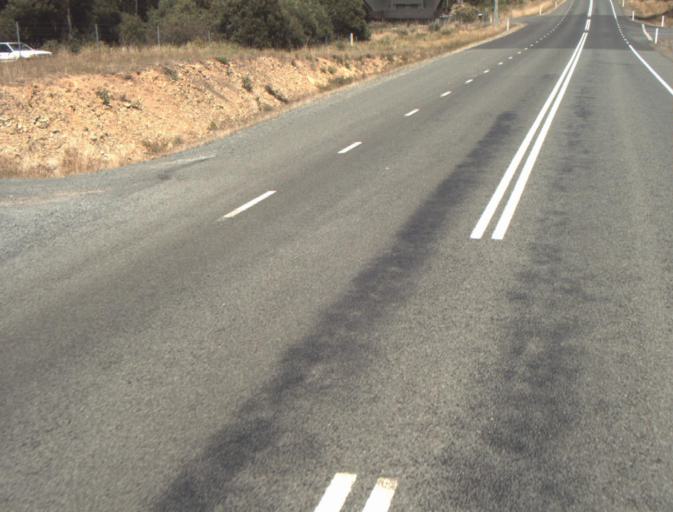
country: AU
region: Tasmania
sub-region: Launceston
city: Newstead
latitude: -41.3337
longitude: 147.3490
